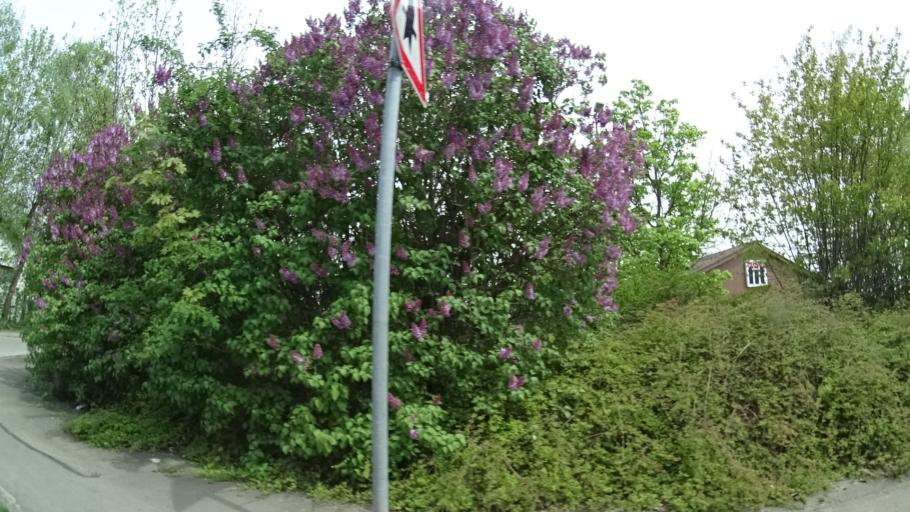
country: DE
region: Baden-Wuerttemberg
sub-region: Freiburg Region
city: Dauchingen
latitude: 48.0625
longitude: 8.5540
